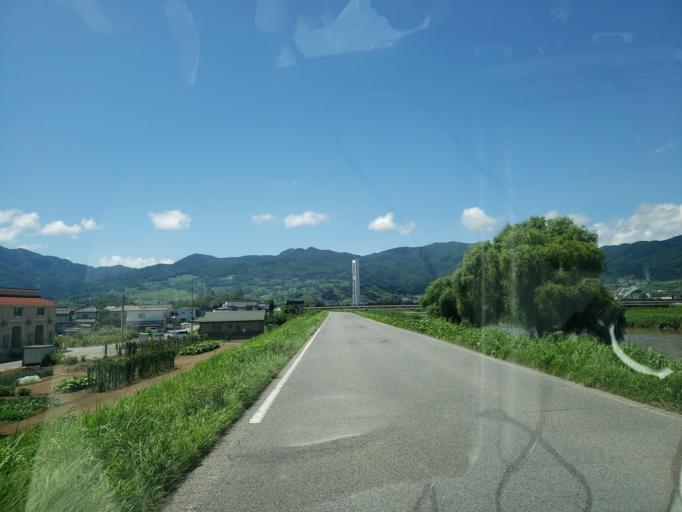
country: JP
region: Nagano
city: Nagano-shi
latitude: 36.5348
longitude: 138.1139
